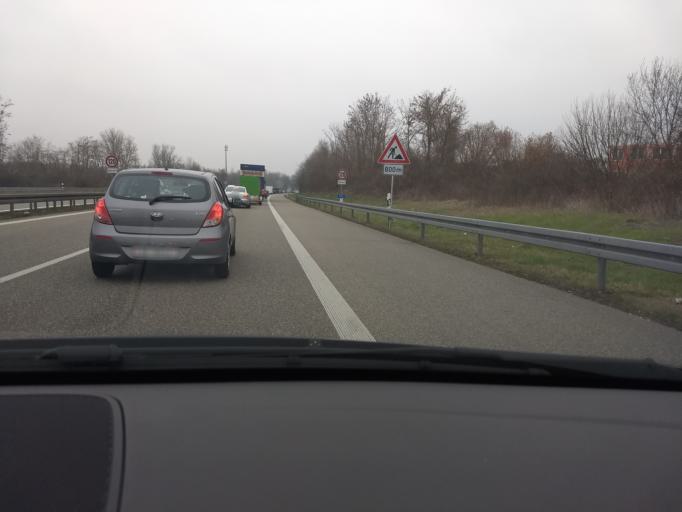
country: FR
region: Alsace
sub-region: Departement du Haut-Rhin
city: Kembs
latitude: 47.7009
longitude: 7.5218
